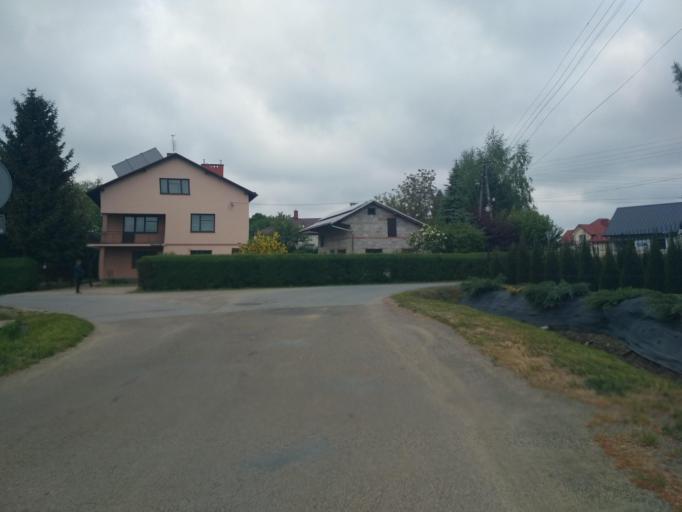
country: PL
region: Subcarpathian Voivodeship
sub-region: Powiat krosnienski
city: Chorkowka
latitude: 49.6647
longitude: 21.7162
